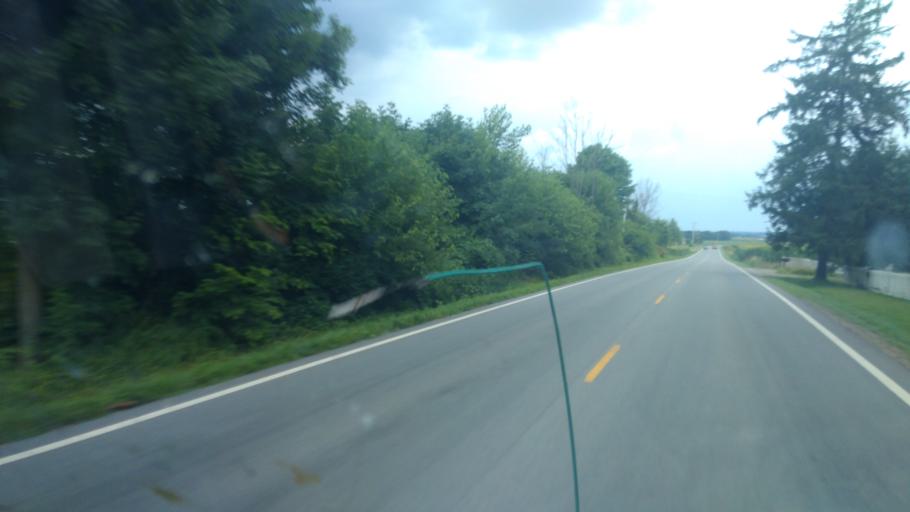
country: US
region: Ohio
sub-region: Fairfield County
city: Millersport
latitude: 39.9041
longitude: -82.5607
